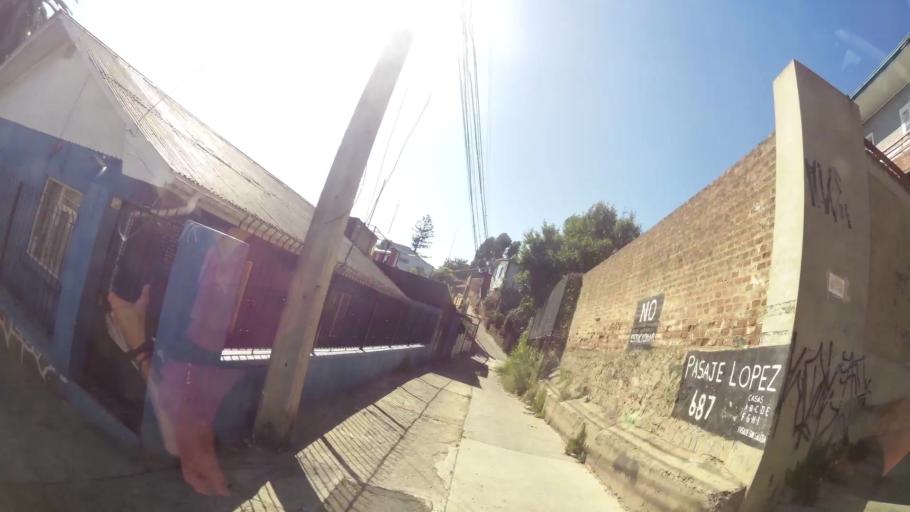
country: CL
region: Valparaiso
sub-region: Provincia de Valparaiso
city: Valparaiso
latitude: -33.0492
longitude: -71.6354
